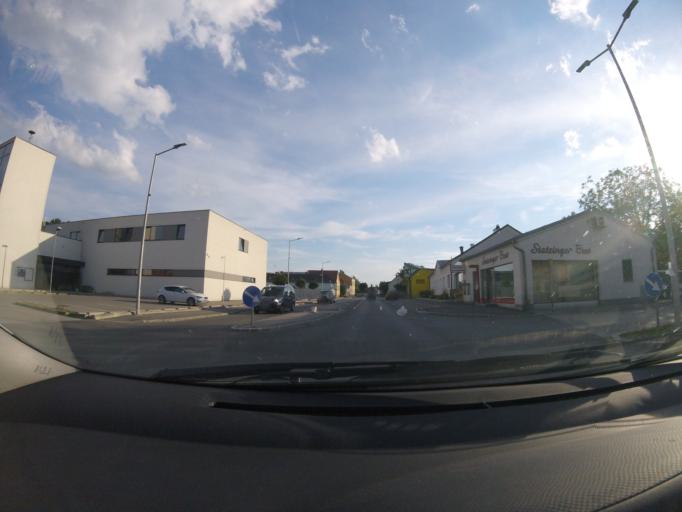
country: AT
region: Lower Austria
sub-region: Politischer Bezirk Wiener Neustadt
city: Zillingdorf
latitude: 47.8572
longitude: 16.3194
